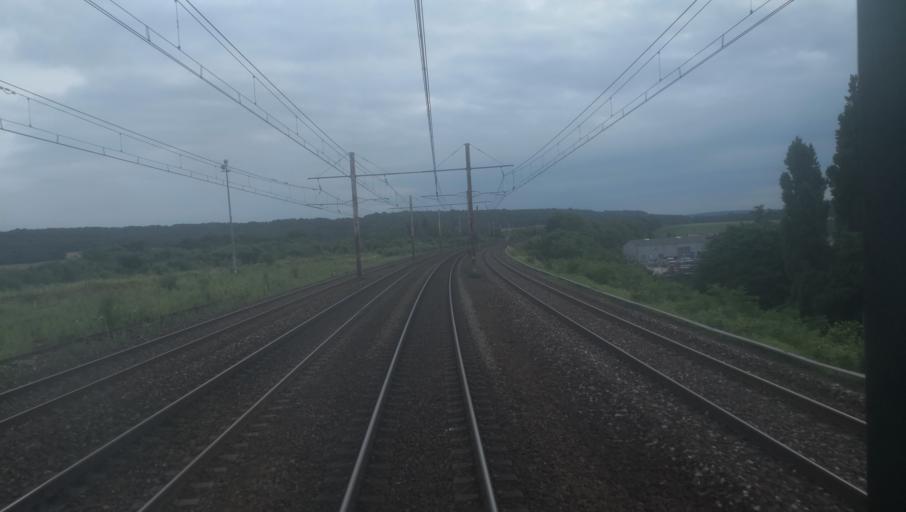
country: FR
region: Ile-de-France
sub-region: Departement de l'Essonne
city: Morigny-Champigny
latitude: 48.4557
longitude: 2.1686
